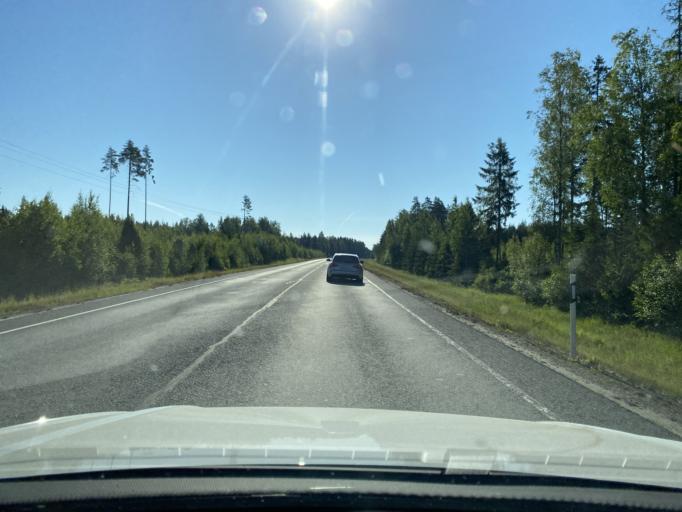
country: FI
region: Haeme
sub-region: Forssa
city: Tammela
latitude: 60.8299
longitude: 23.8677
